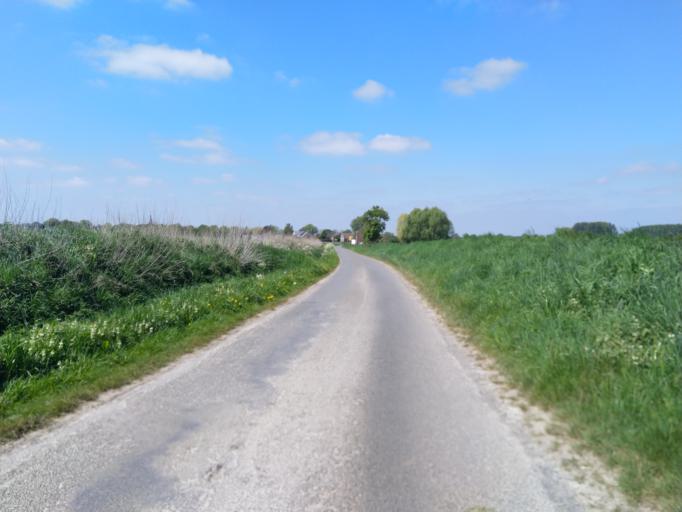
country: BE
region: Wallonia
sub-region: Province du Hainaut
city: Chievres
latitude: 50.5285
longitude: 3.8076
